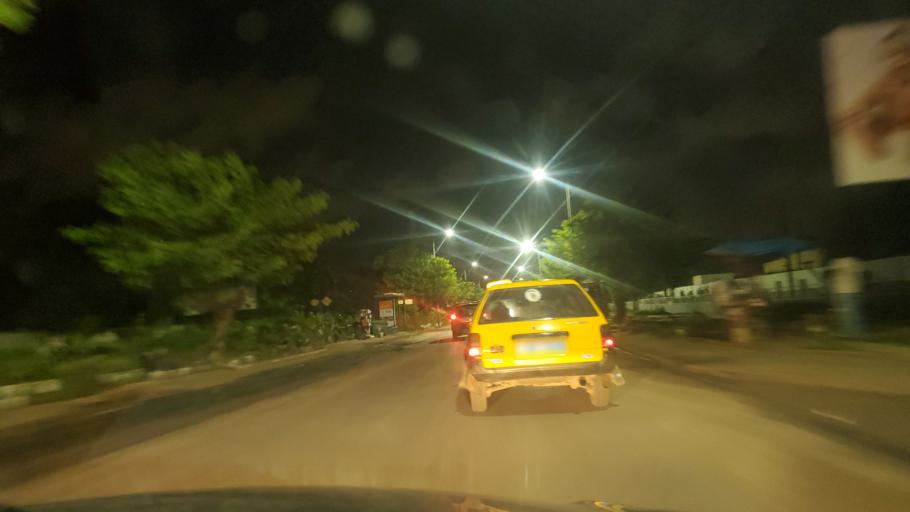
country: SN
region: Dakar
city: Mermoz Boabab
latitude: 14.6997
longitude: -17.4667
